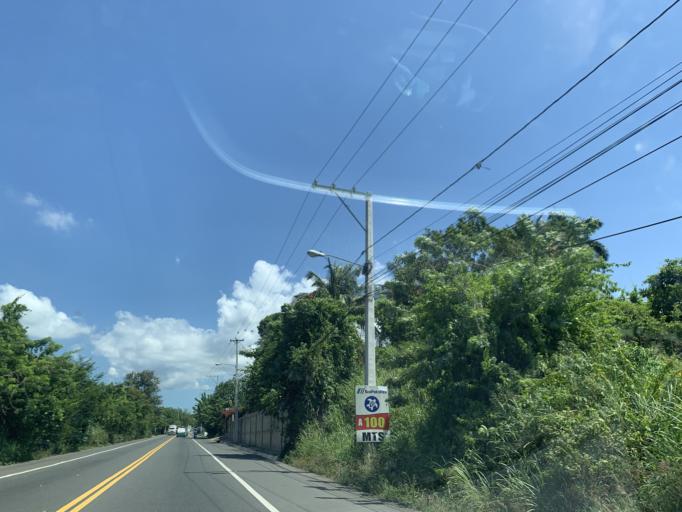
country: DO
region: Puerto Plata
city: Imbert
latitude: 19.7311
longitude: -70.8298
